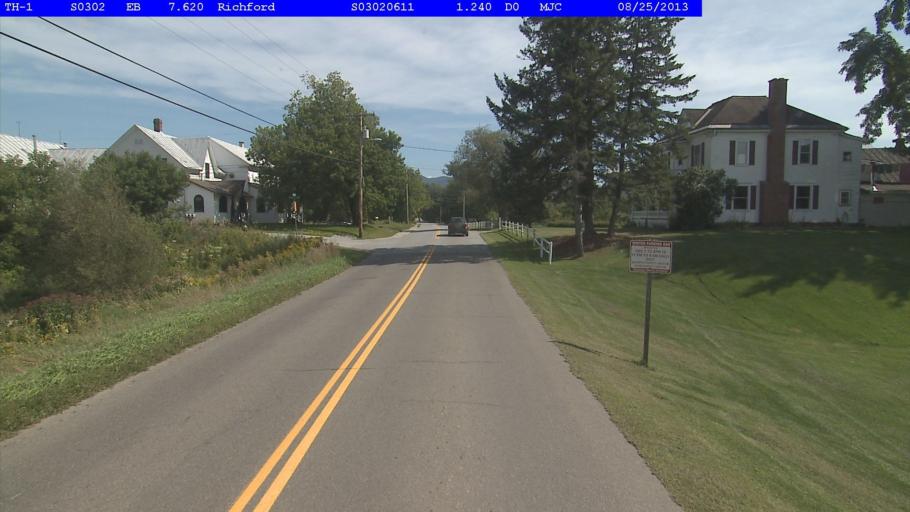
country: US
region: Vermont
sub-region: Franklin County
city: Richford
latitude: 44.9999
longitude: -72.6783
